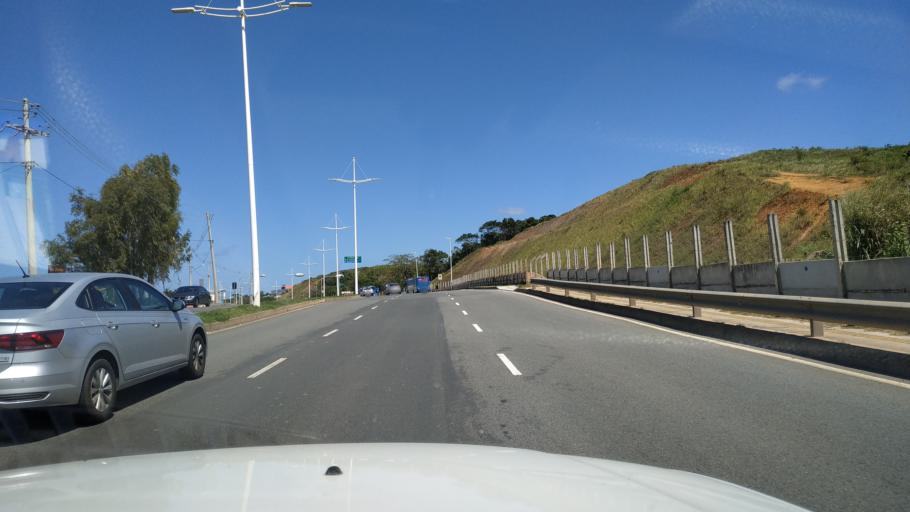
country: BR
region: Bahia
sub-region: Lauro De Freitas
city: Lauro de Freitas
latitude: -12.9328
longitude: -38.3836
